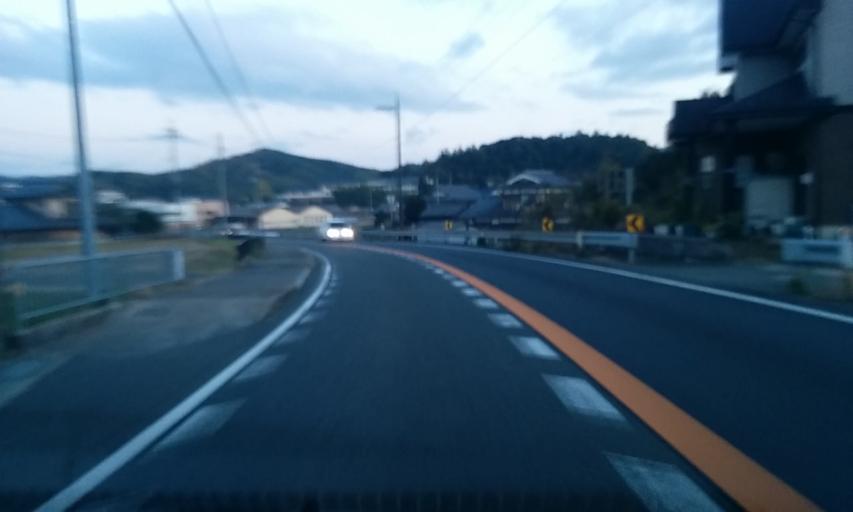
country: JP
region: Kyoto
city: Kameoka
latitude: 35.1127
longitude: 135.4645
